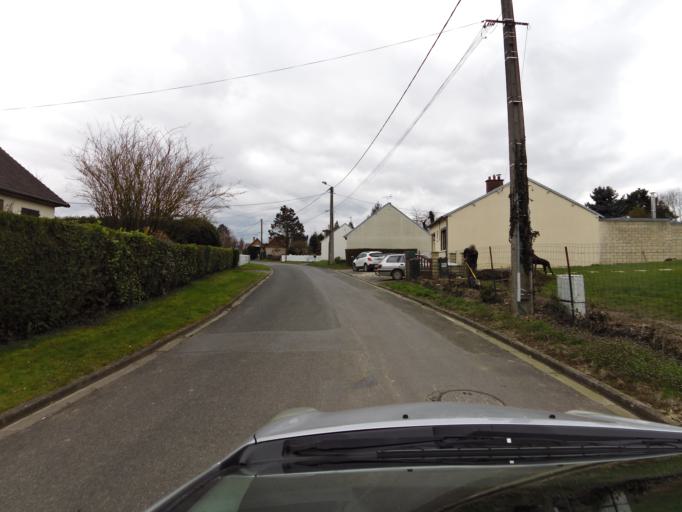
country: FR
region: Picardie
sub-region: Departement de la Somme
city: Bray-sur-Somme
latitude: 49.9092
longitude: 2.8036
